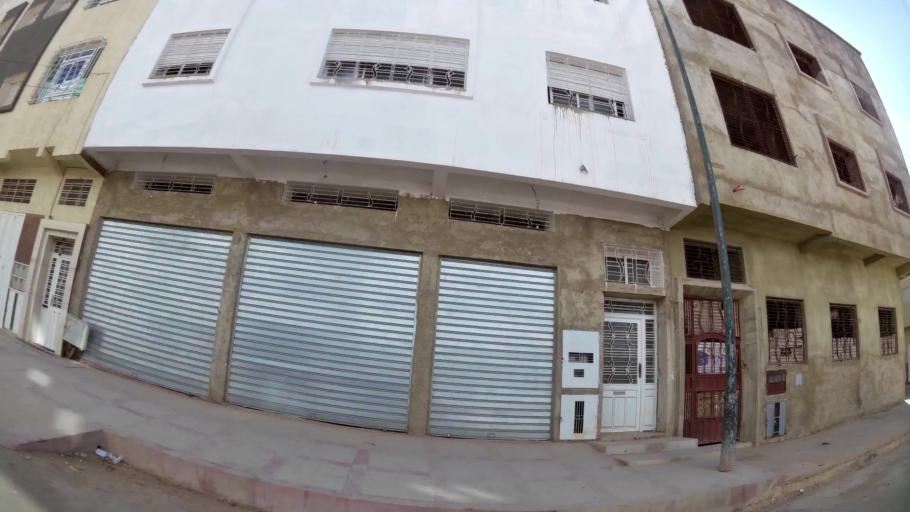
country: MA
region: Meknes-Tafilalet
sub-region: Meknes
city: Meknes
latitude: 33.8744
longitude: -5.5852
